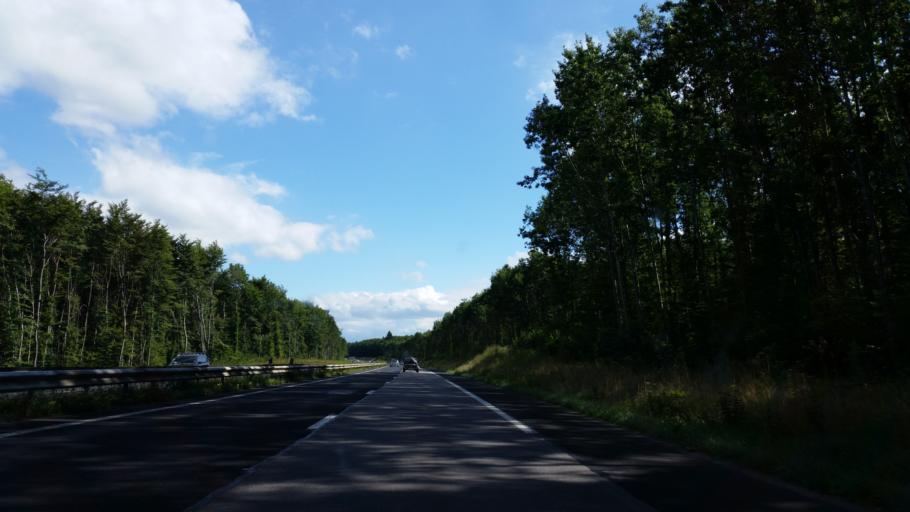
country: FR
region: Lorraine
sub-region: Departement des Vosges
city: Igney
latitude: 48.2816
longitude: 6.3790
